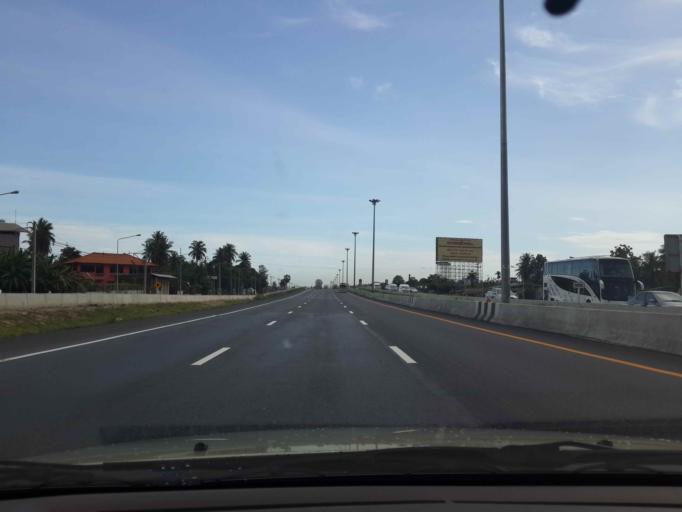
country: TH
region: Chon Buri
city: Ban Talat Bueng
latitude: 13.0156
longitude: 100.9964
